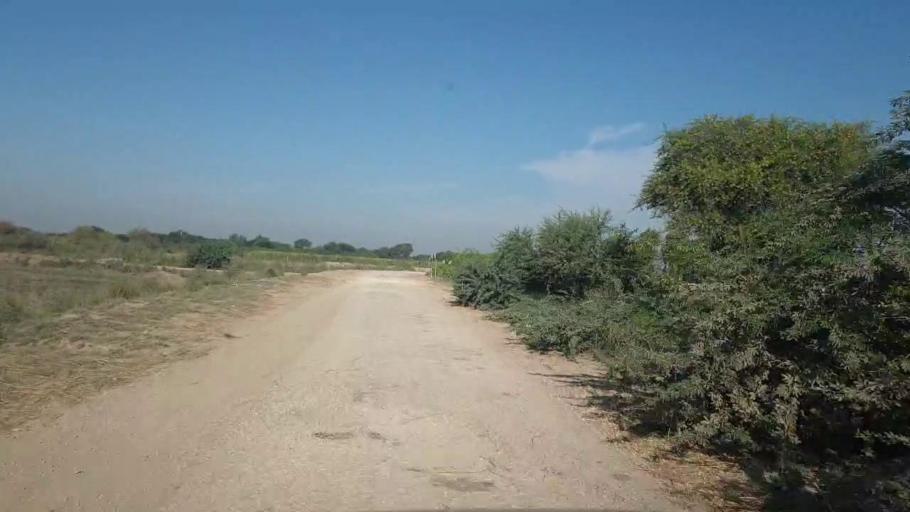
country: PK
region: Sindh
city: Talhar
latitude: 24.9330
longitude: 68.7923
